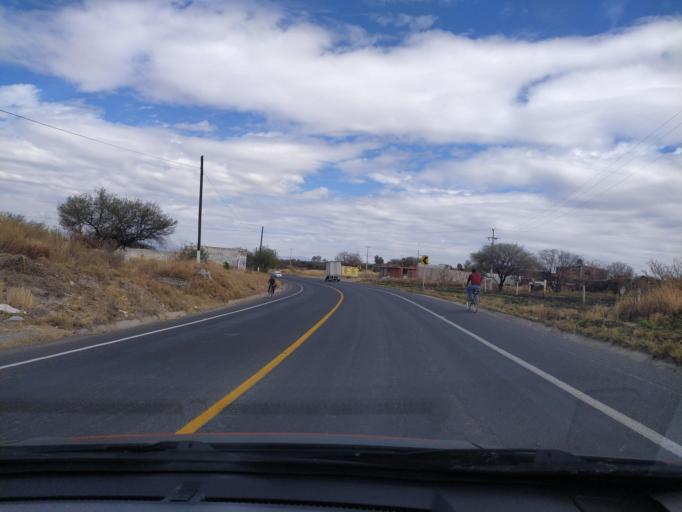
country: LA
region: Oudomxai
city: Muang La
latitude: 20.9938
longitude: 101.8374
